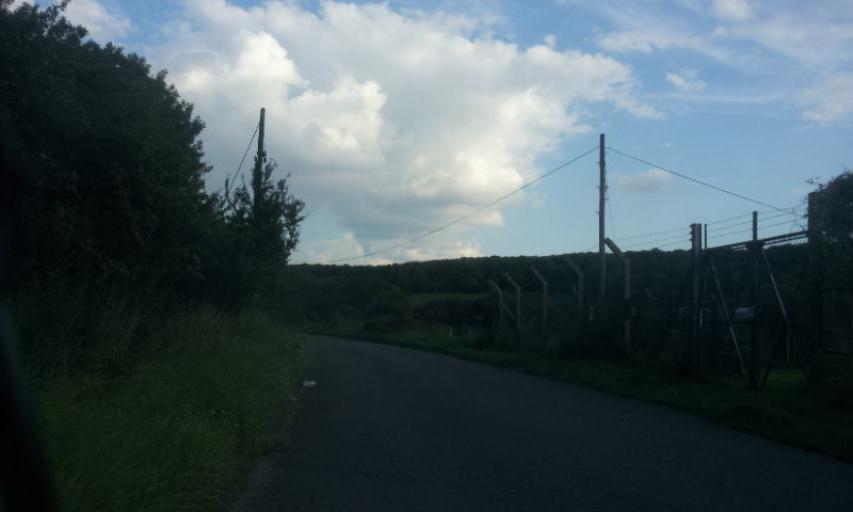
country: GB
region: England
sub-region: Medway
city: Cuxton
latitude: 51.3785
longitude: 0.4251
